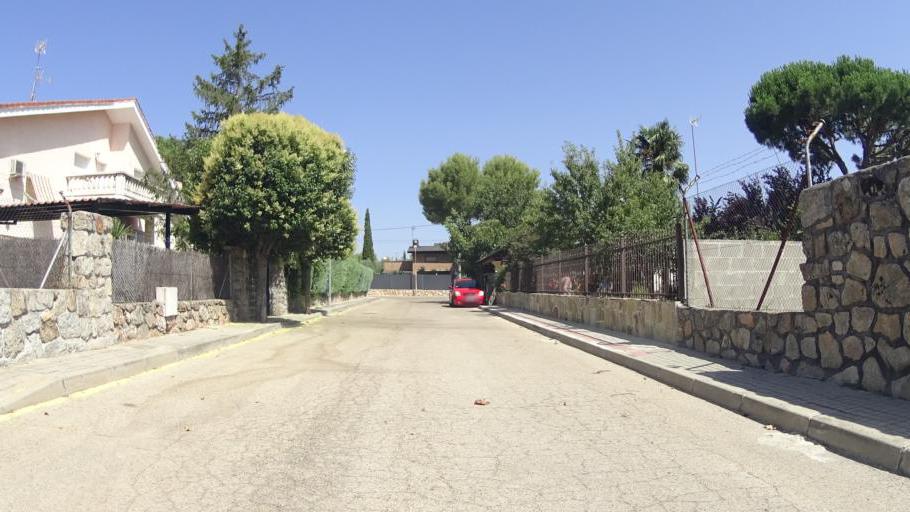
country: ES
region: Madrid
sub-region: Provincia de Madrid
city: Colmenarejo
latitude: 40.5595
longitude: -4.0067
